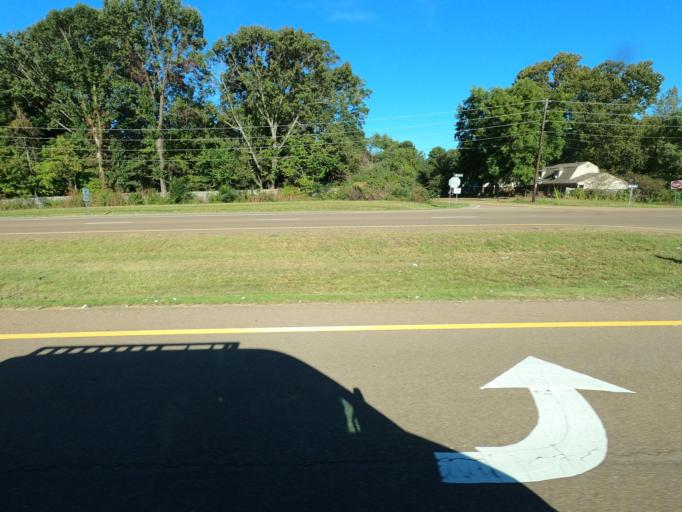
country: US
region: Tennessee
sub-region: Tipton County
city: Brighton
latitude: 35.4887
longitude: -89.7334
